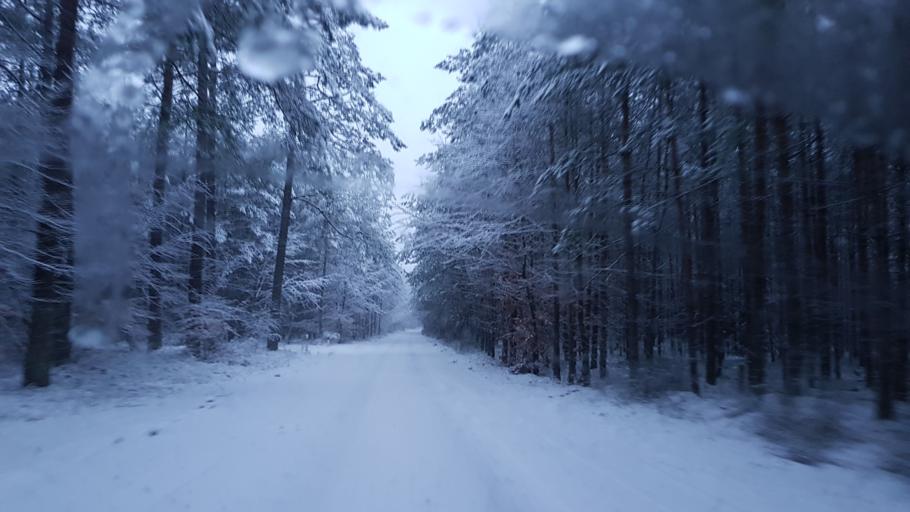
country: PL
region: West Pomeranian Voivodeship
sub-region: Powiat koszalinski
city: Polanow
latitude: 54.1677
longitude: 16.4869
